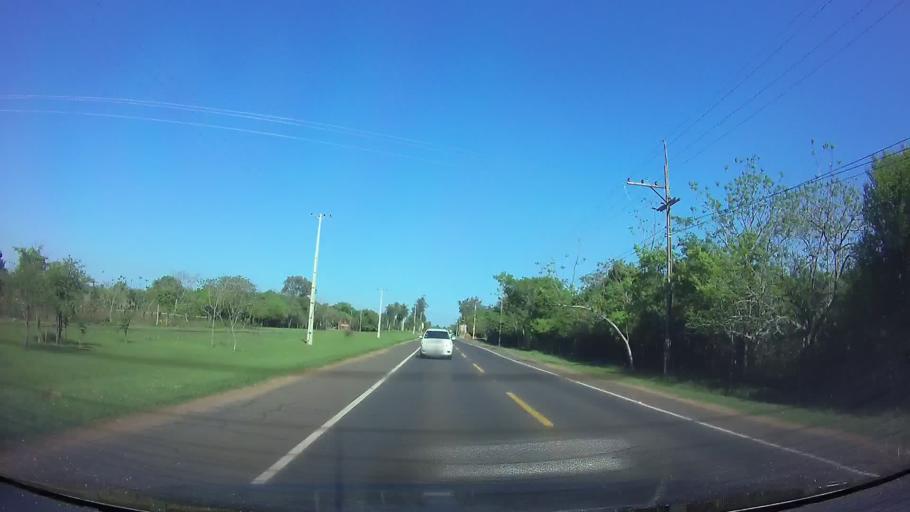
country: PY
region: Central
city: Itaugua
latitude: -25.3641
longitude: -57.3157
